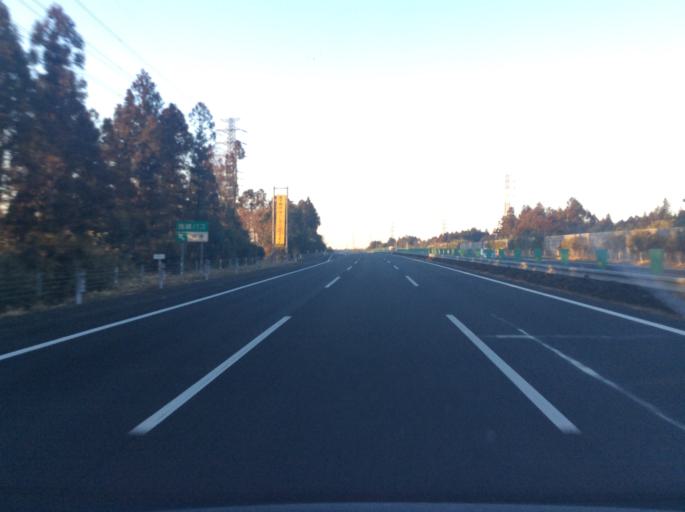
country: JP
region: Ibaraki
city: Tomobe
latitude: 36.3517
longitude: 140.3692
